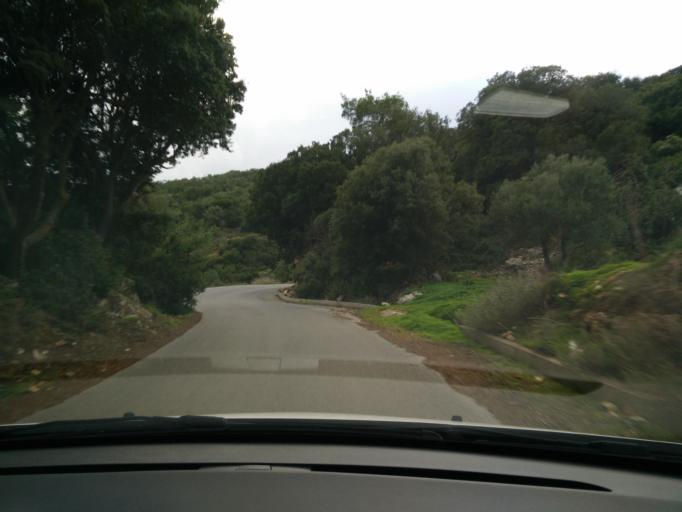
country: GR
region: Crete
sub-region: Nomos Lasithiou
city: Kritsa
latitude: 35.1017
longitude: 25.6926
